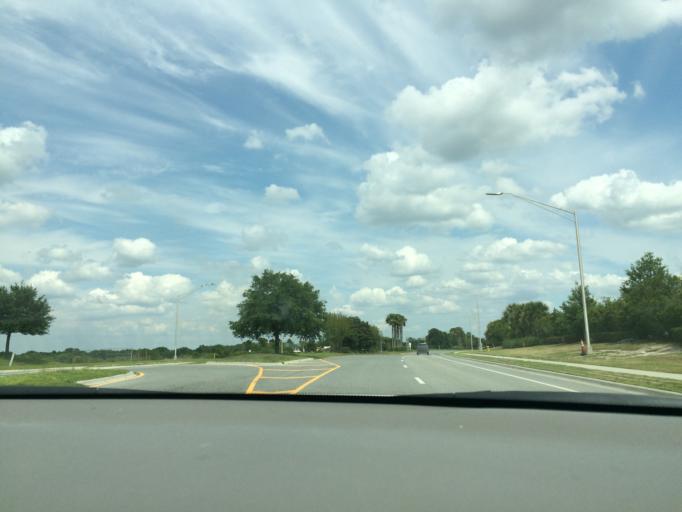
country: US
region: Florida
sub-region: Sarasota County
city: The Meadows
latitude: 27.4602
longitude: -82.4212
